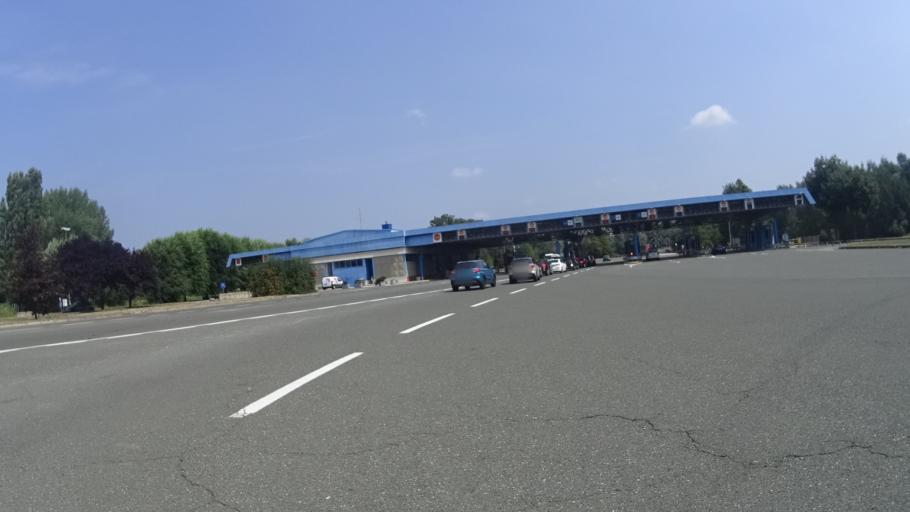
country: HR
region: Medimurska
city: Gorican
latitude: 46.4175
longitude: 16.6892
